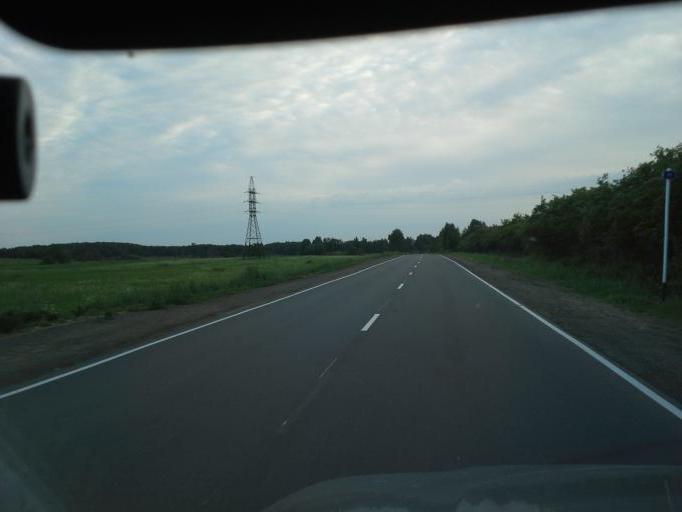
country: RU
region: Ivanovo
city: Petrovskiy
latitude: 56.6243
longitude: 40.2760
